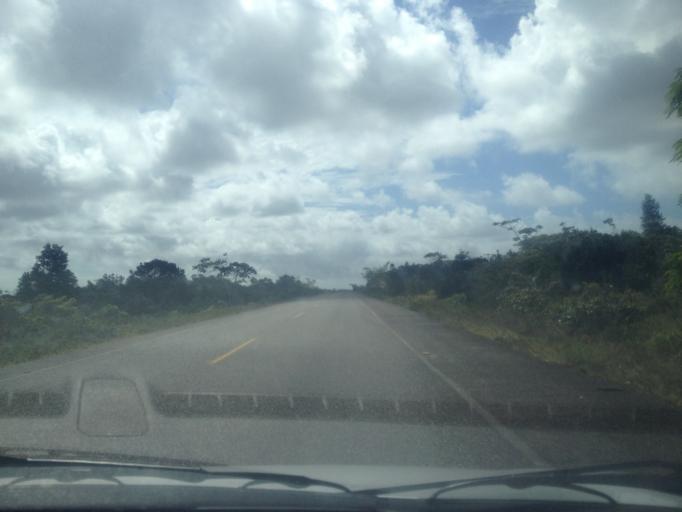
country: BR
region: Bahia
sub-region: Entre Rios
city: Entre Rios
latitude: -12.2545
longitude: -37.8645
